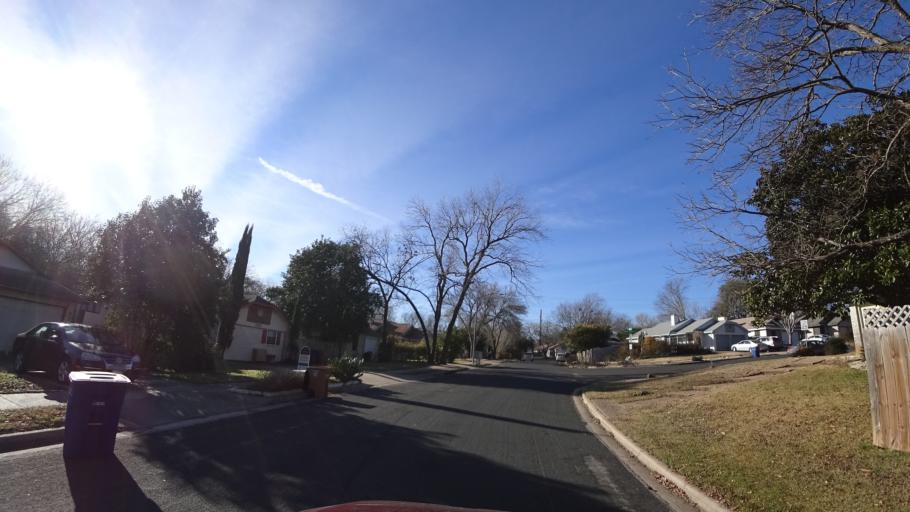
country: US
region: Texas
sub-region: Travis County
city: Wells Branch
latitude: 30.3962
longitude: -97.7008
